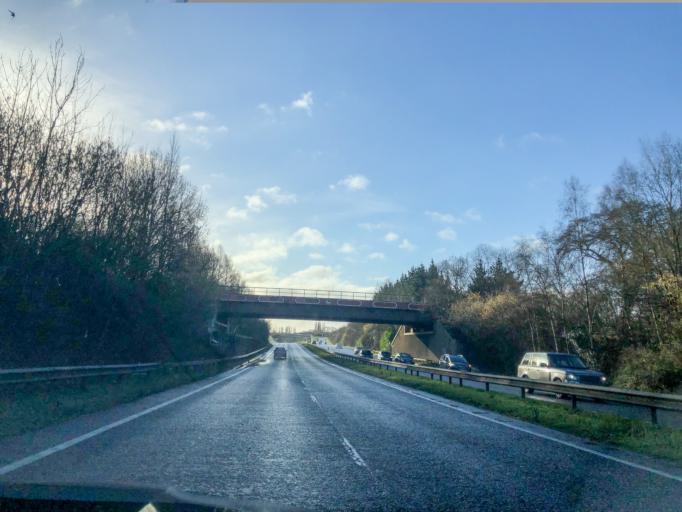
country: GB
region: England
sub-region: Hampshire
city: Farnborough
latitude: 51.3001
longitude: -0.7399
